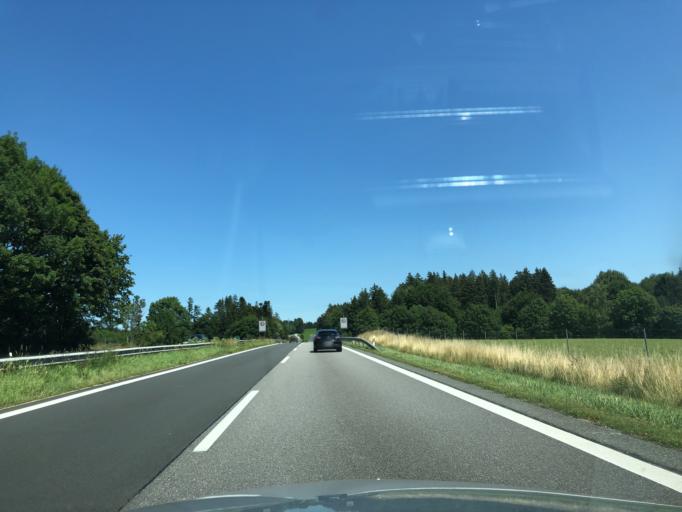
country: DE
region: Bavaria
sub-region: Upper Bavaria
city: Aschau im Chiemgau
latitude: 47.8036
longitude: 12.3235
